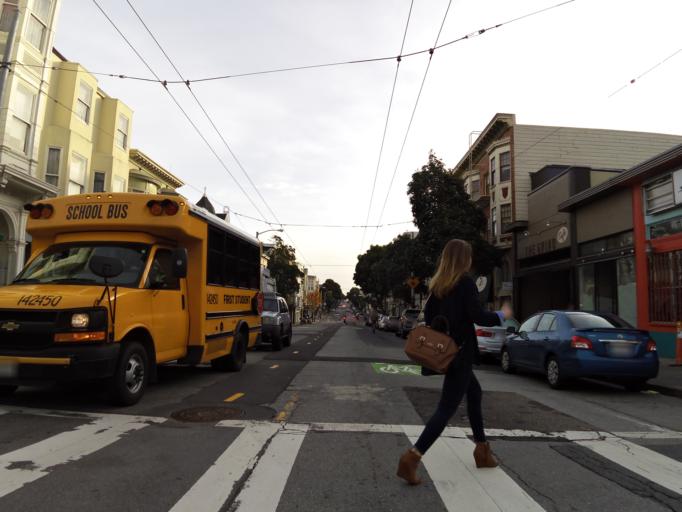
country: US
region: California
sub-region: San Francisco County
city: San Francisco
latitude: 37.7715
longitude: -122.4354
